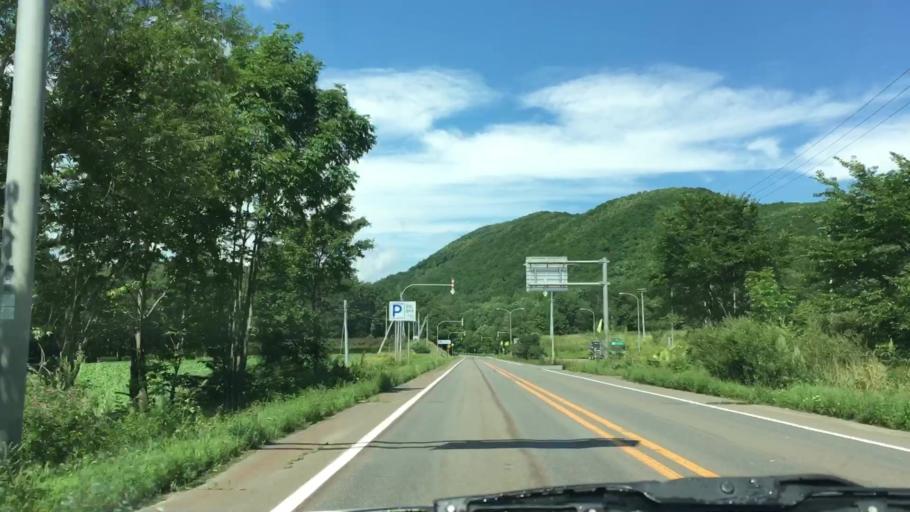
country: JP
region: Hokkaido
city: Otofuke
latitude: 43.2413
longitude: 143.4847
